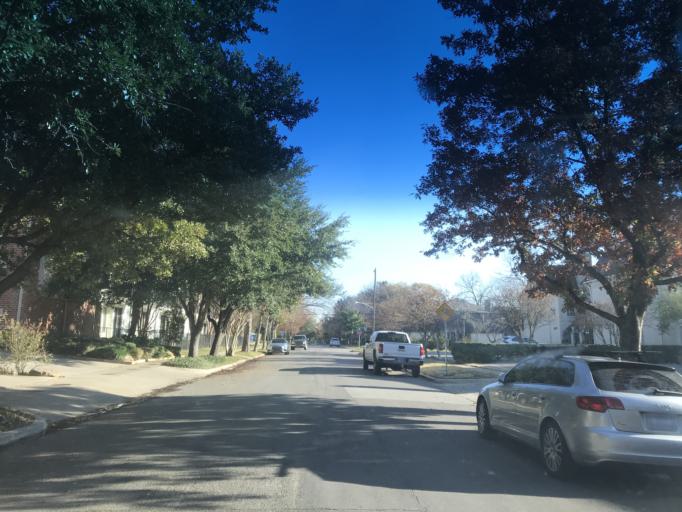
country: US
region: Texas
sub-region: Dallas County
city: Highland Park
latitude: 32.8210
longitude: -96.8128
